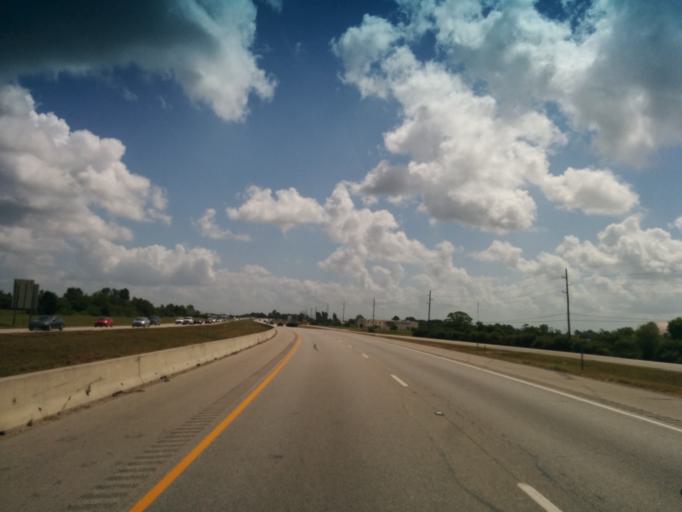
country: US
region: Texas
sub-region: Austin County
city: Sealy
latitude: 29.7686
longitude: -96.1401
